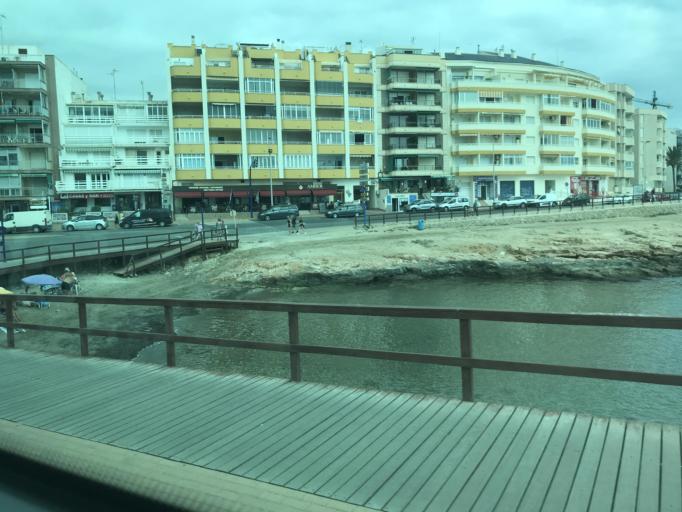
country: ES
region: Valencia
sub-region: Provincia de Alicante
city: Torrevieja
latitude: 37.9802
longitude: -0.6641
